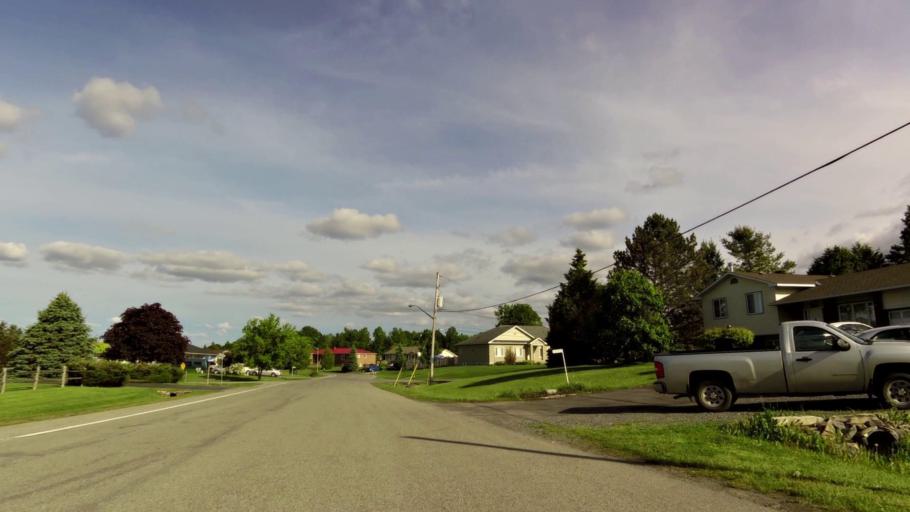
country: CA
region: Ontario
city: Ottawa
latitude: 45.2656
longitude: -75.5664
